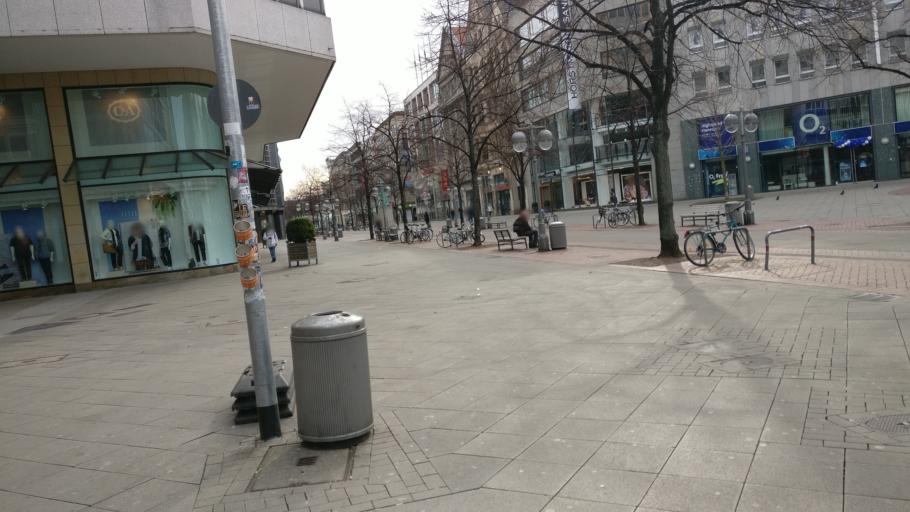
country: DE
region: Lower Saxony
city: Hannover
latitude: 52.3756
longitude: 9.7346
